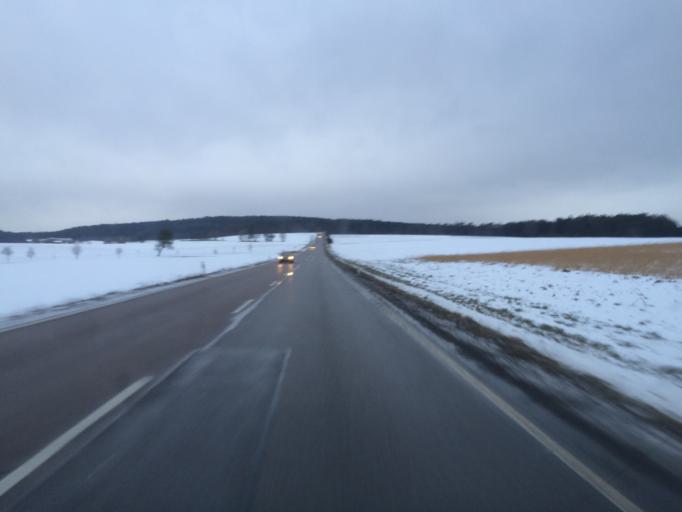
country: DE
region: Bavaria
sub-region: Upper Palatinate
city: Breitenbrunn
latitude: 49.3545
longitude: 12.0616
